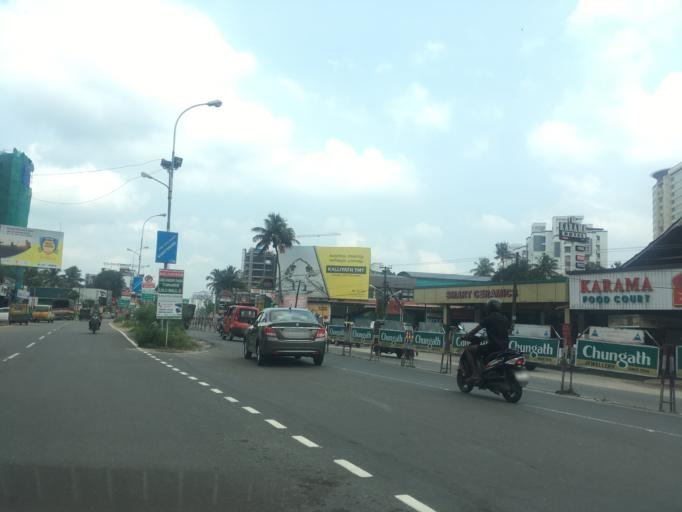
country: IN
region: Kerala
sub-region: Ernakulam
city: Elur
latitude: 10.0267
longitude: 76.3060
